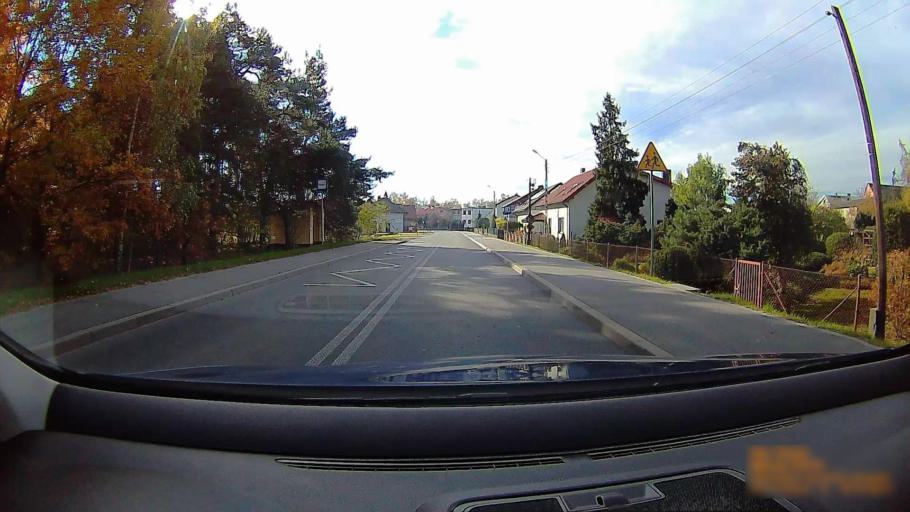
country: PL
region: Greater Poland Voivodeship
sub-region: Powiat ostrzeszowski
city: Doruchow
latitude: 51.3649
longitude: 18.0293
